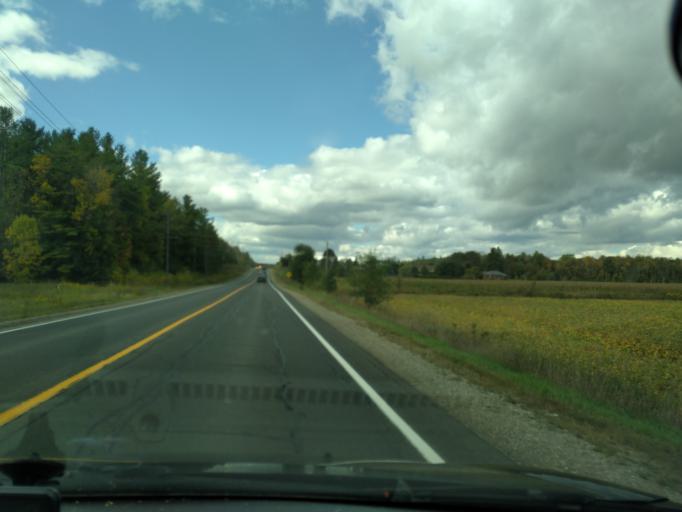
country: CA
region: Ontario
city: Angus
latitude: 44.2547
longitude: -79.7944
